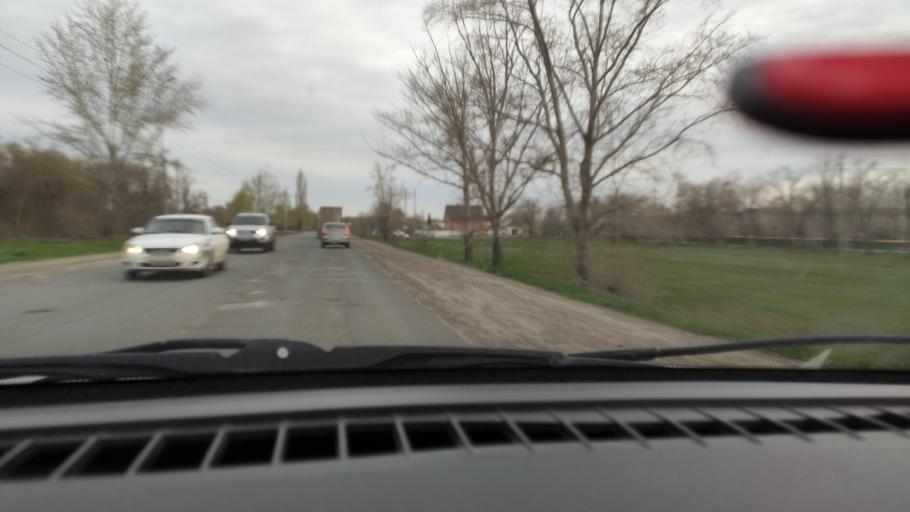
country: RU
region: Orenburg
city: Tatarskaya Kargala
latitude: 51.8649
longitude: 55.1390
